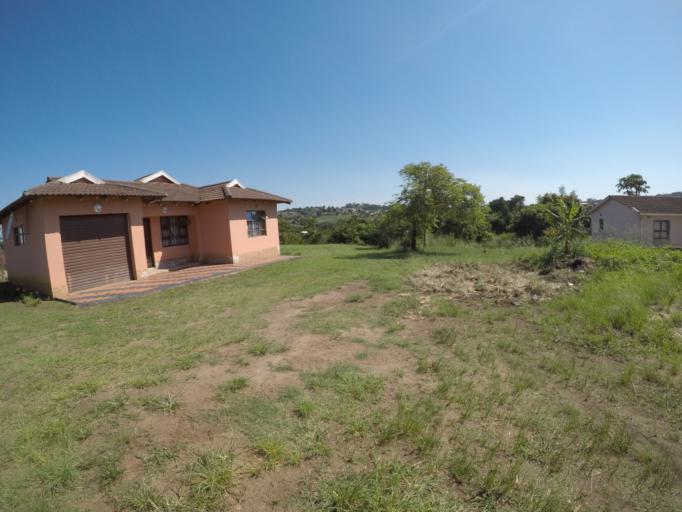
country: ZA
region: KwaZulu-Natal
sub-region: uThungulu District Municipality
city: Empangeni
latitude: -28.7777
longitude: 31.8786
